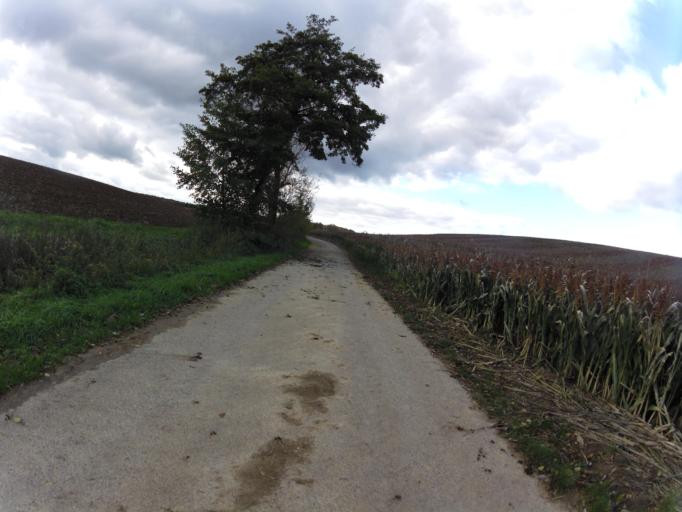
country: DE
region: Bavaria
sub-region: Regierungsbezirk Unterfranken
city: Kurnach
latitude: 49.8752
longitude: 10.0067
